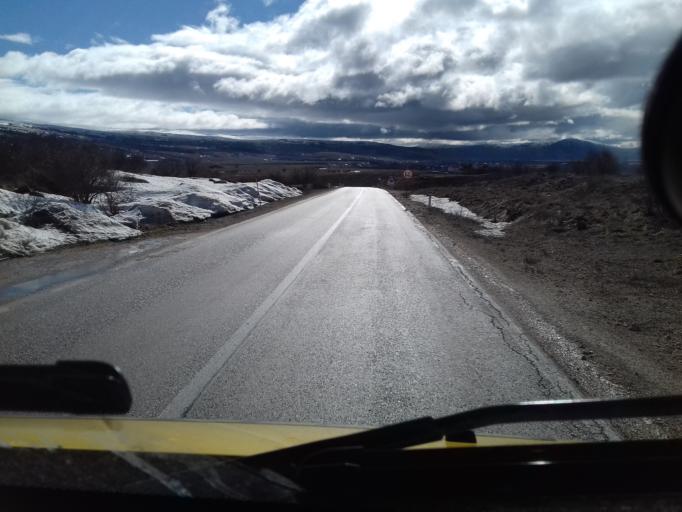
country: BA
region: Federation of Bosnia and Herzegovina
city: Tomislavgrad
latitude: 43.7679
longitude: 17.2353
